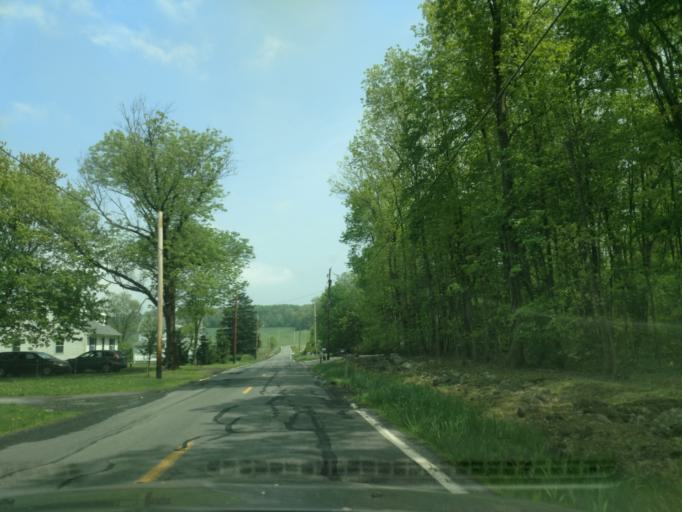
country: US
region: Pennsylvania
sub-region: Chester County
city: Elverson
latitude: 40.1697
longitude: -75.8387
